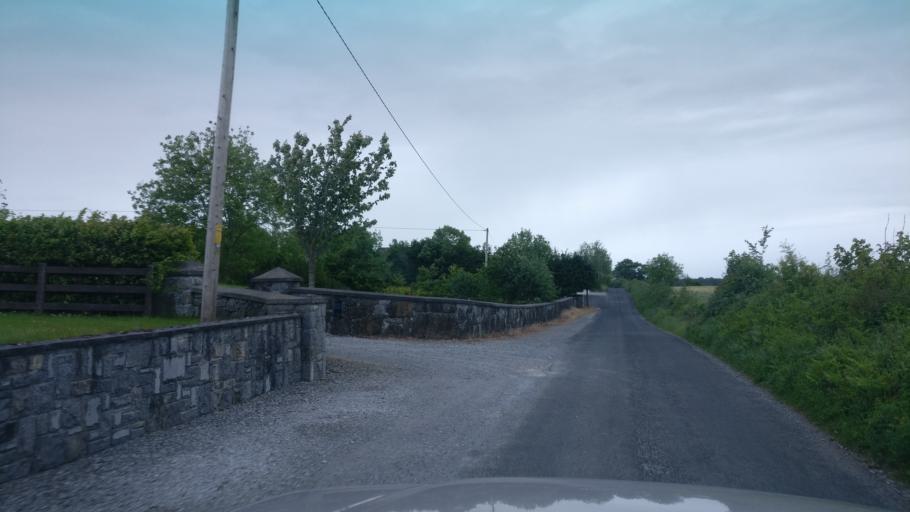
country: IE
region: Connaught
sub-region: County Galway
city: Loughrea
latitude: 53.1233
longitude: -8.4285
